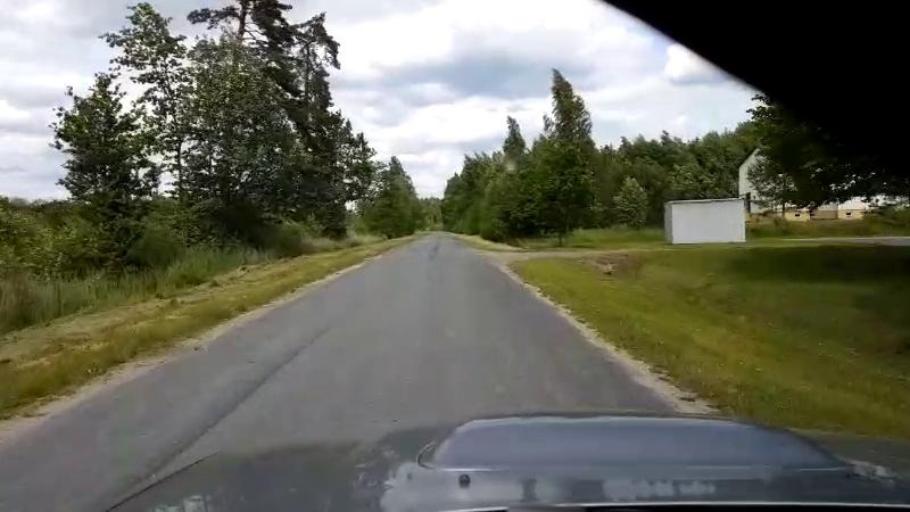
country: EE
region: Paernumaa
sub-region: Halinga vald
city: Parnu-Jaagupi
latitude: 58.5203
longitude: 24.5641
